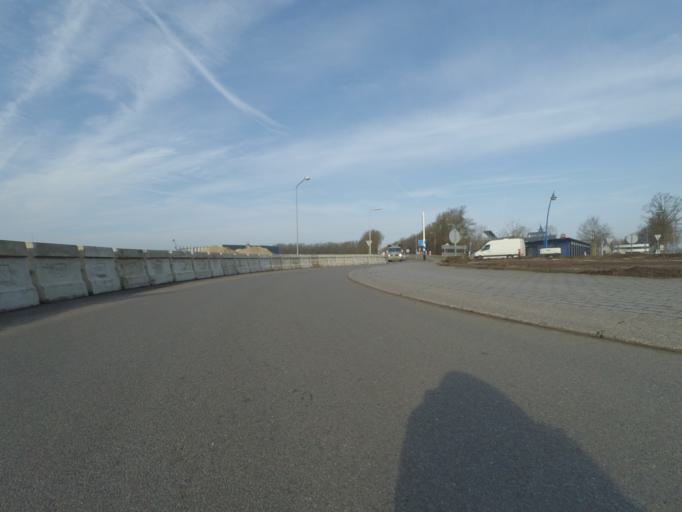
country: NL
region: Gelderland
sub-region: Gemeente Barneveld
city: Barneveld
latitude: 52.1496
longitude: 5.5687
